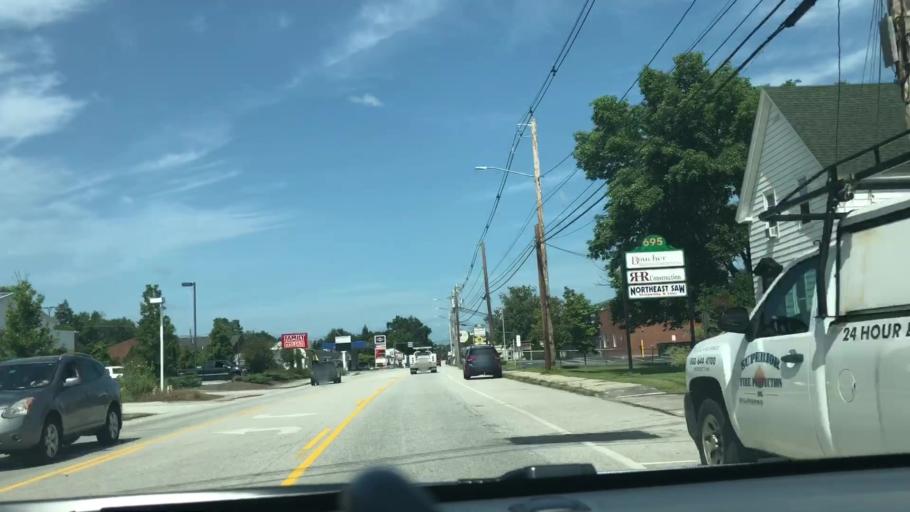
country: US
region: New Hampshire
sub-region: Hillsborough County
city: Pinardville
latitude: 42.9928
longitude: -71.5046
